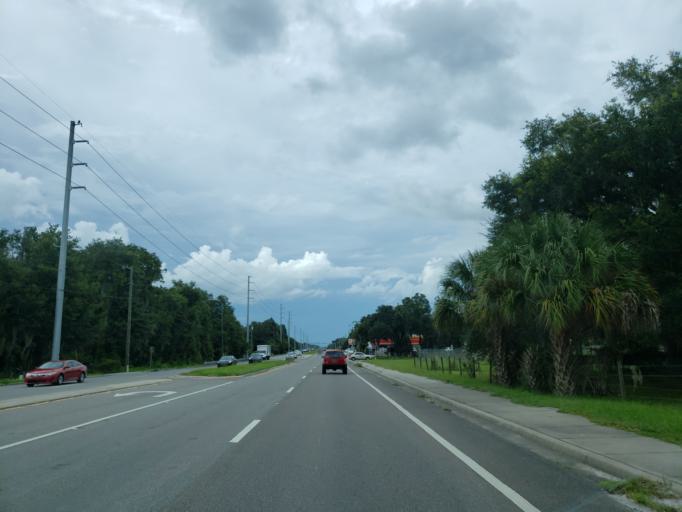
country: US
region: Florida
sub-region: Polk County
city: Willow Oak
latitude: 27.9477
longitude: -82.0553
